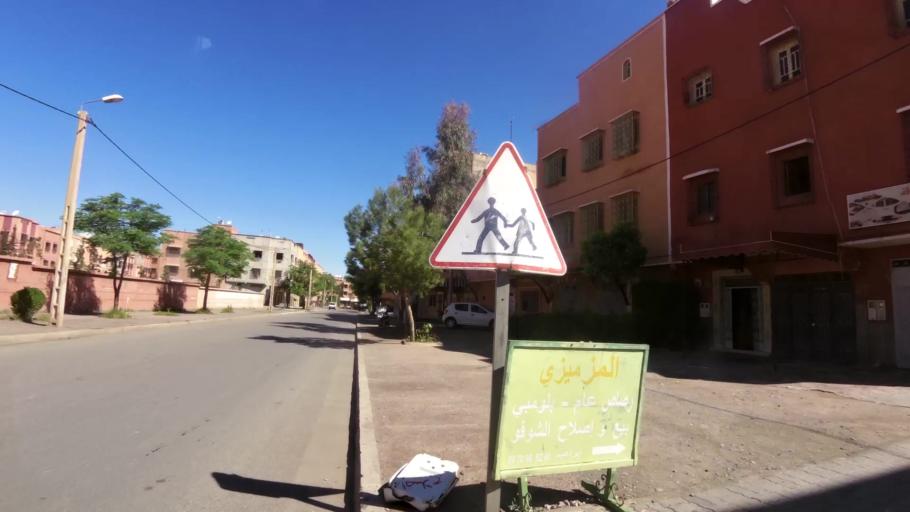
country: MA
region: Marrakech-Tensift-Al Haouz
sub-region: Marrakech
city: Marrakesh
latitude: 31.5943
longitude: -8.0465
